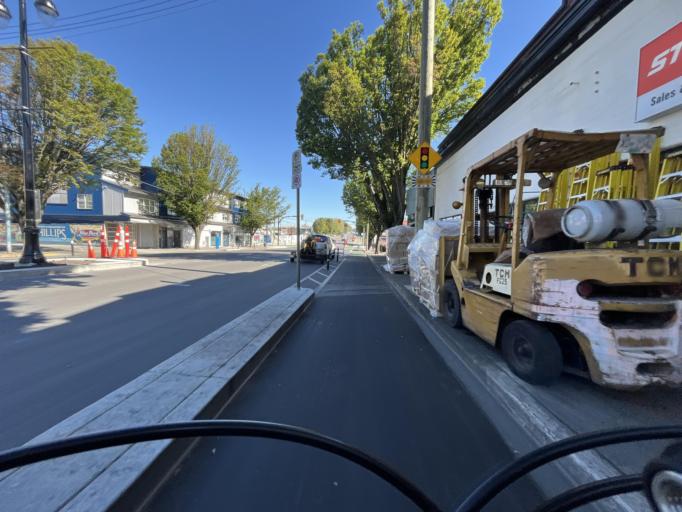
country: CA
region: British Columbia
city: Victoria
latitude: 48.4321
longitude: -123.3671
